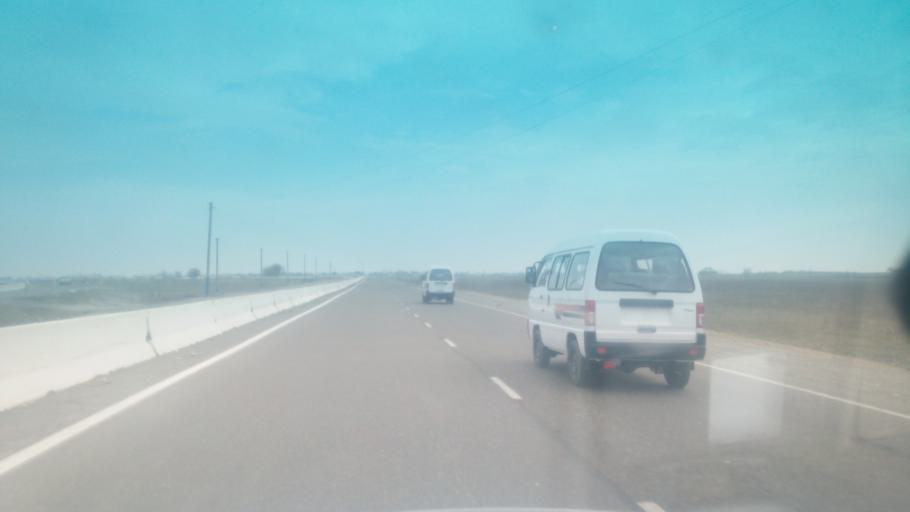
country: KZ
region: Ongtustik Qazaqstan
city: Myrzakent
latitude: 40.5018
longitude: 68.5410
